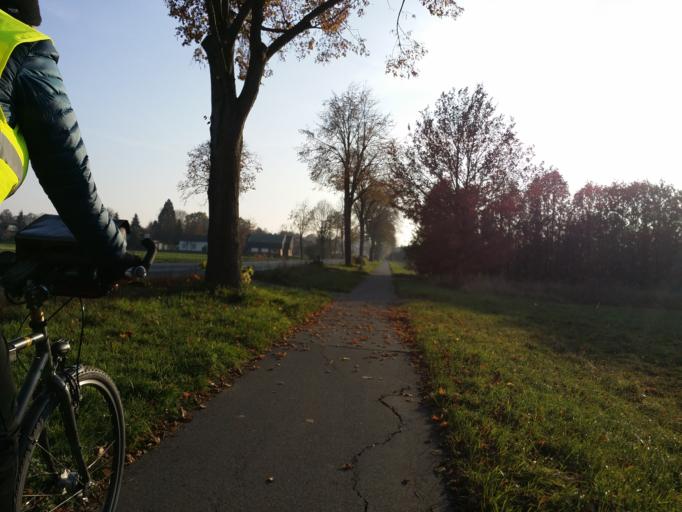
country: DE
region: Lower Saxony
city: Ottersberg
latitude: 53.1175
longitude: 9.1415
